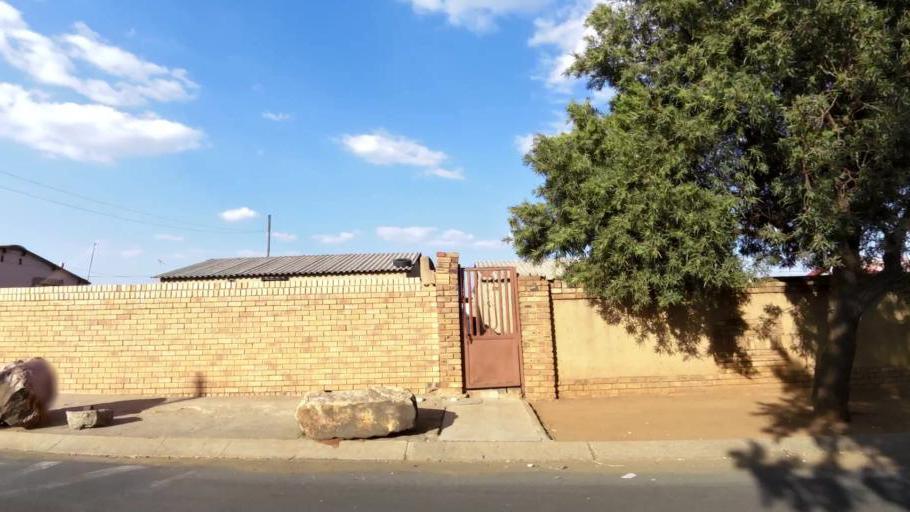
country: ZA
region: Gauteng
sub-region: City of Johannesburg Metropolitan Municipality
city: Roodepoort
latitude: -26.2090
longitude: 27.8774
